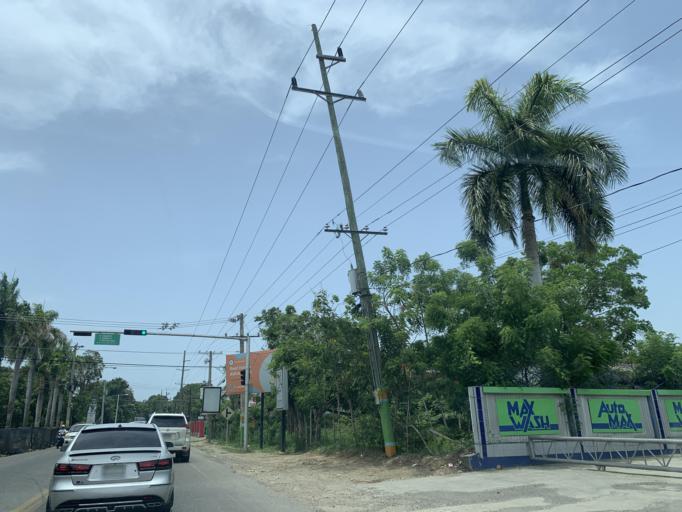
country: DO
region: Puerto Plata
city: Cabarete
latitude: 19.7648
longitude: -70.5111
